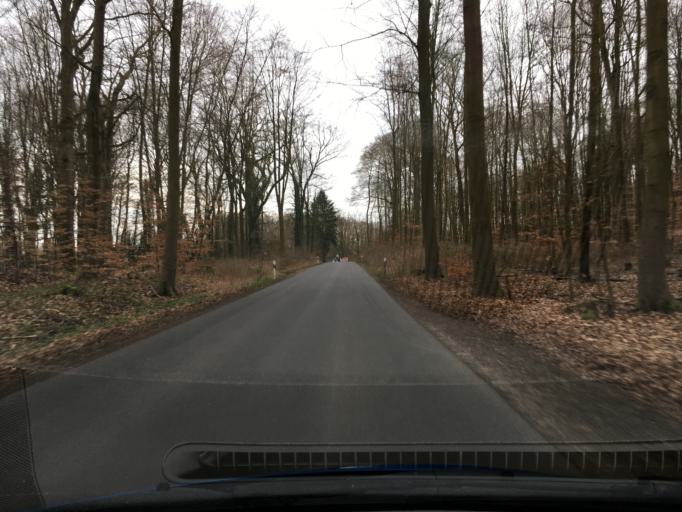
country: DE
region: Lower Saxony
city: Bad Bevensen
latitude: 53.0845
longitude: 10.5626
